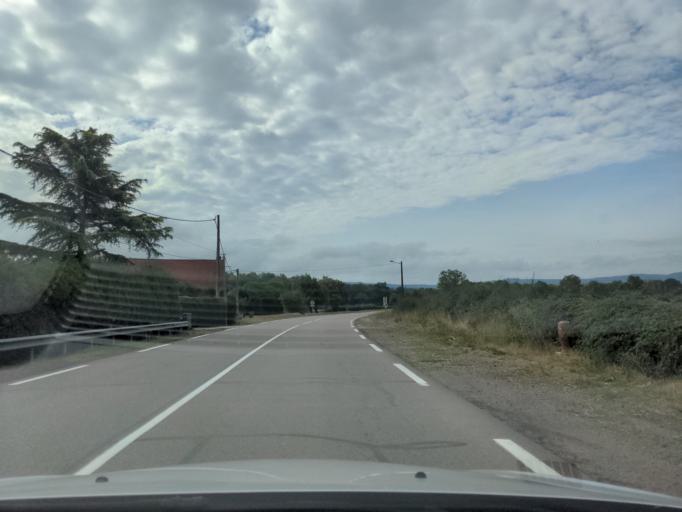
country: FR
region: Bourgogne
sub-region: Departement de Saone-et-Loire
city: Autun
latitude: 47.0062
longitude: 4.3212
